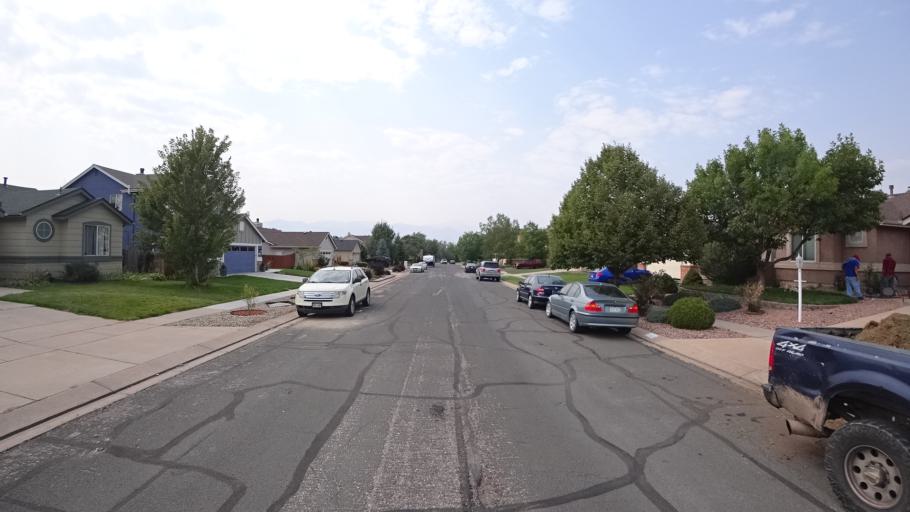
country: US
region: Colorado
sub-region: El Paso County
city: Cimarron Hills
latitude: 38.8204
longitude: -104.7409
